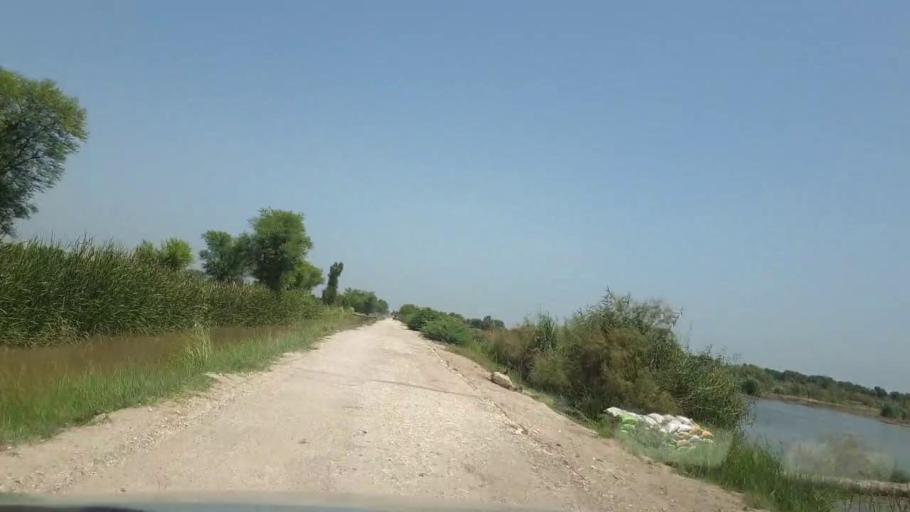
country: PK
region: Sindh
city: Rohri
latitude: 27.6400
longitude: 69.1027
